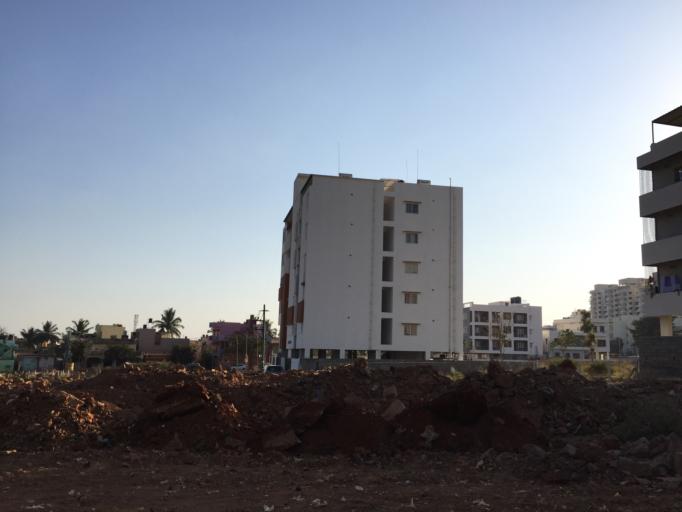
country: IN
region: Karnataka
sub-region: Bangalore Urban
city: Yelahanka
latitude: 13.0599
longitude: 77.6321
